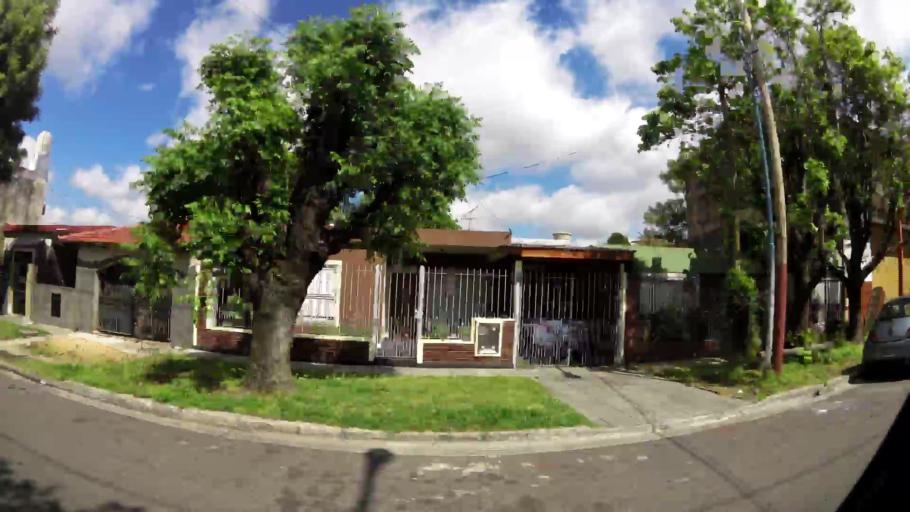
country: AR
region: Buenos Aires
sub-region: Partido de Lanus
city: Lanus
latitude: -34.6762
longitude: -58.4151
